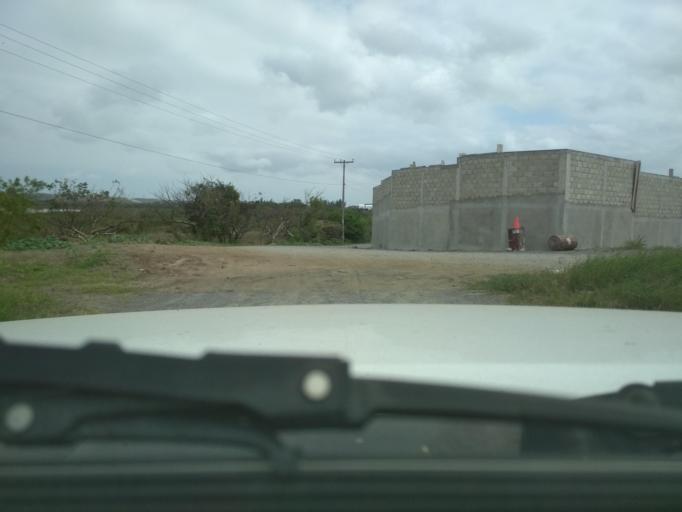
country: MX
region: Veracruz
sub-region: Veracruz
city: Delfino Victoria (Santa Fe)
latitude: 19.2442
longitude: -96.2575
